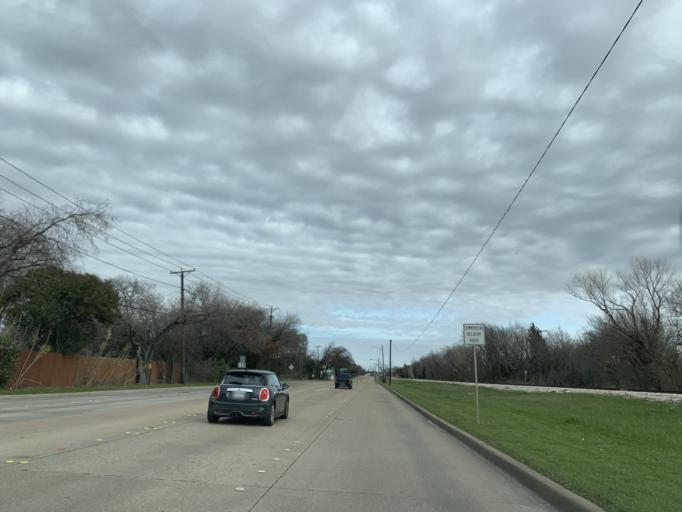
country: US
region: Texas
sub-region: Tarrant County
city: Edgecliff Village
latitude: 32.6928
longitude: -97.3622
